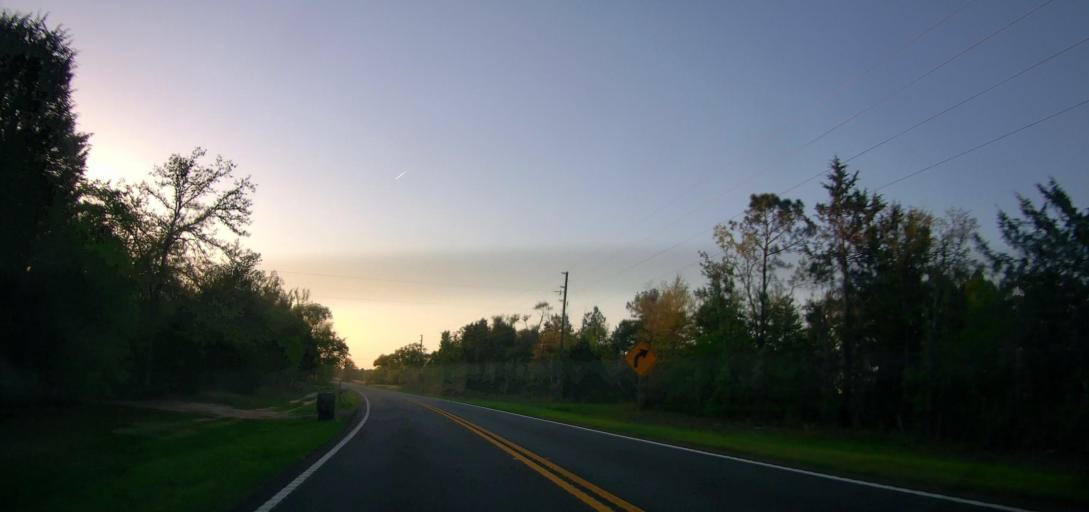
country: US
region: Georgia
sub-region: Marion County
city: Buena Vista
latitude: 32.4556
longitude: -84.6270
